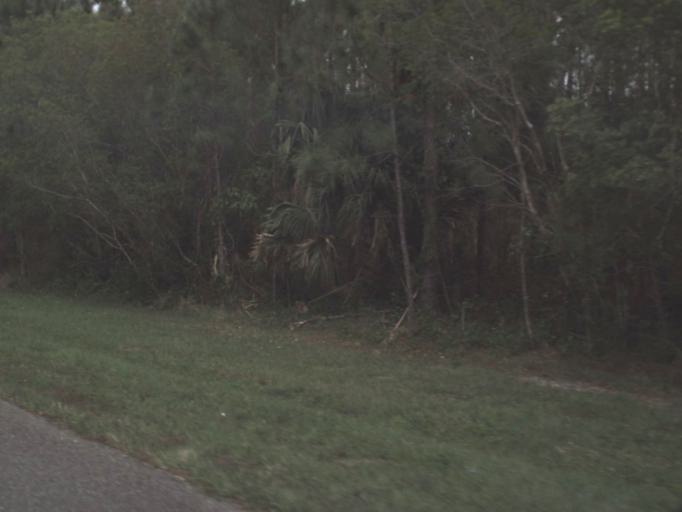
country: US
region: Florida
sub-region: Flagler County
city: Bunnell
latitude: 29.4122
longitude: -81.3049
